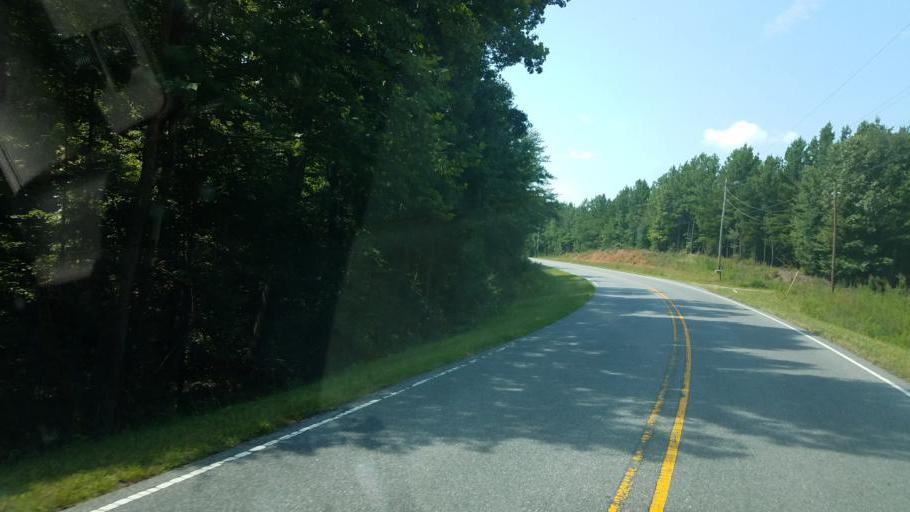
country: US
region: North Carolina
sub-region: Burke County
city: Icard
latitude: 35.5645
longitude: -81.5146
